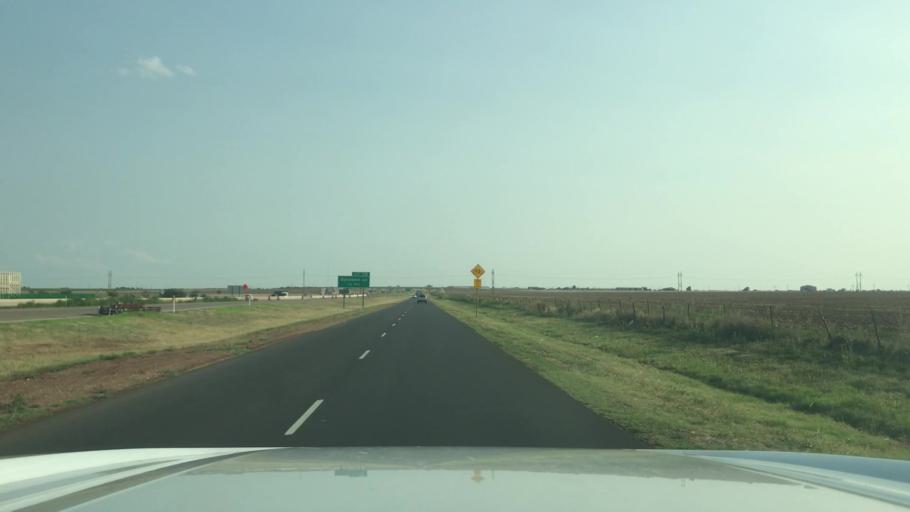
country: US
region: Texas
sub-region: Randall County
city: Canyon
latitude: 35.1116
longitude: -101.9113
